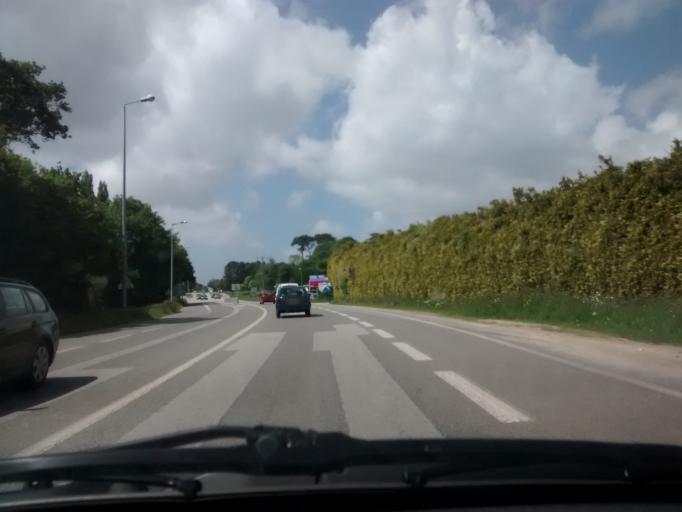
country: FR
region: Brittany
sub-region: Departement du Morbihan
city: Arradon
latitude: 47.6453
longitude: -2.8106
